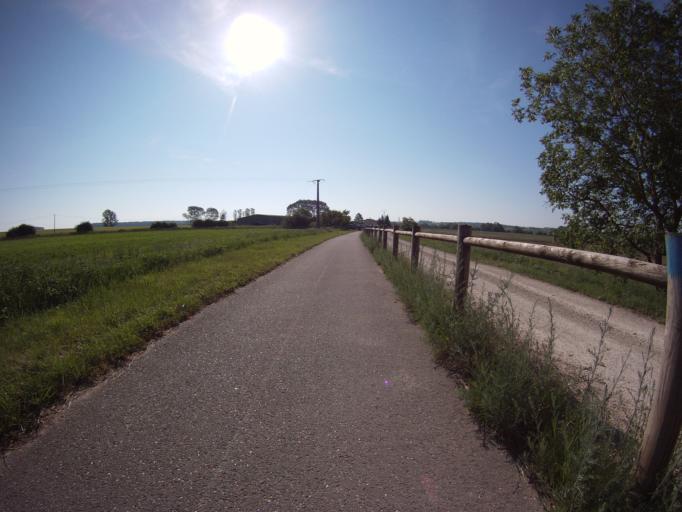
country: FR
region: Lorraine
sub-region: Departement de Meurthe-et-Moselle
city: Bouxieres-aux-Chenes
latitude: 48.7429
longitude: 6.2841
